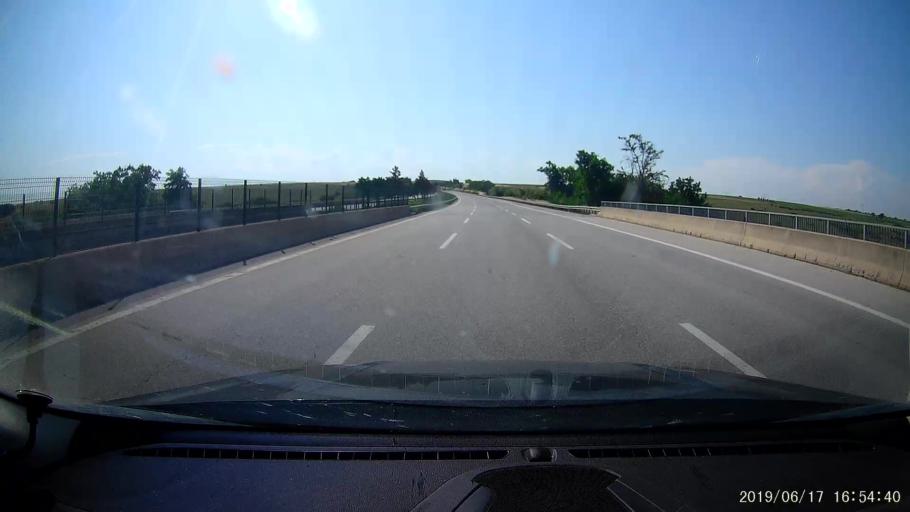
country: TR
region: Kirklareli
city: Inece
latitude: 41.5756
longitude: 26.9889
